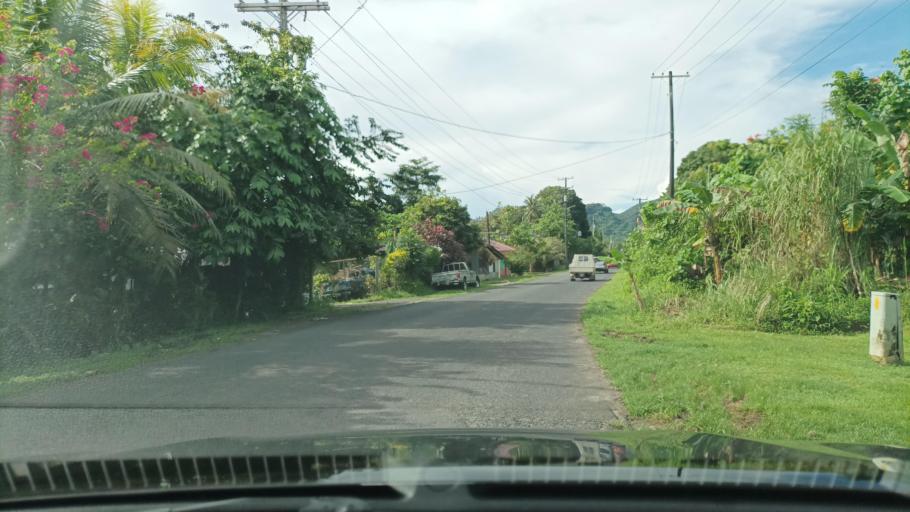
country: FM
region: Pohnpei
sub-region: Kolonia Municipality
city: Kolonia Town
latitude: 6.9478
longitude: 158.1951
